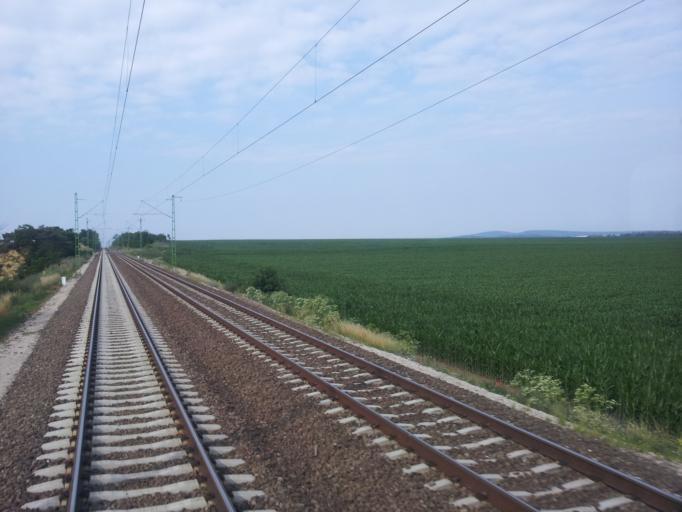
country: HU
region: Fejer
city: Baracska
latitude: 47.2858
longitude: 18.7404
